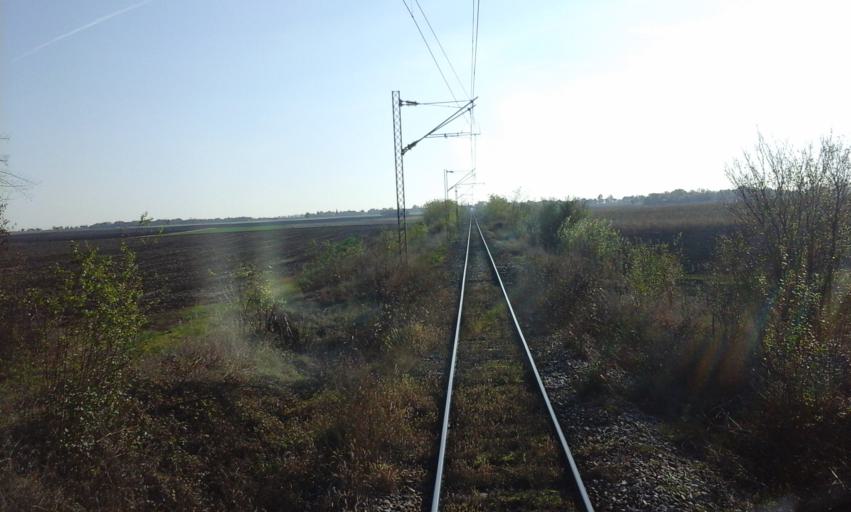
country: RS
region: Autonomna Pokrajina Vojvodina
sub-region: Severnobacki Okrug
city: Mali Igos
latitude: 45.7582
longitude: 19.6485
